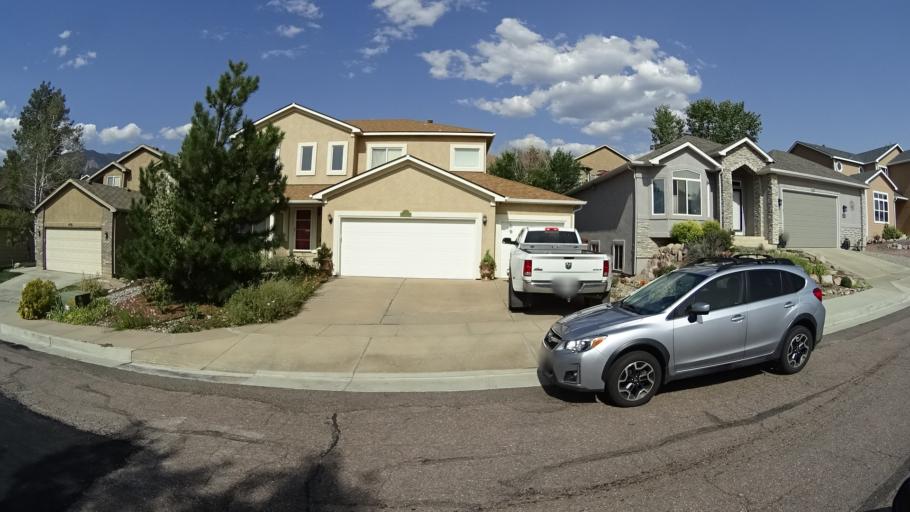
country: US
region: Colorado
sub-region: El Paso County
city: Colorado Springs
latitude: 38.8260
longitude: -104.8545
